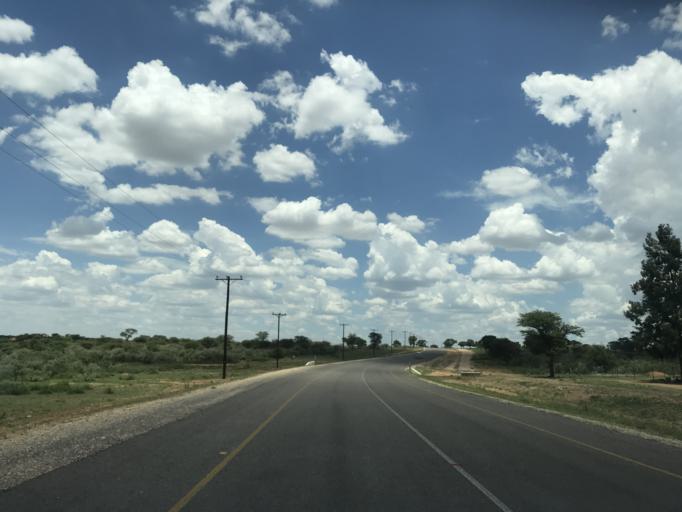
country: BW
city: Mabuli
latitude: -25.7308
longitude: 24.9984
